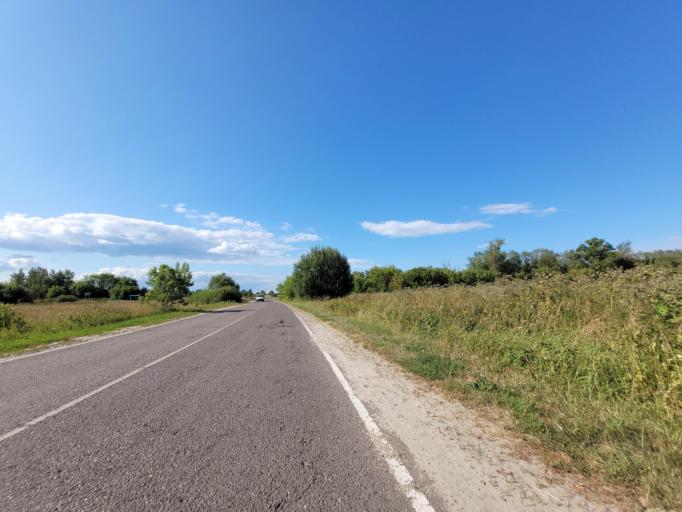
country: RU
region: Moskovskaya
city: Konobeyevo
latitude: 55.4033
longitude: 38.7082
